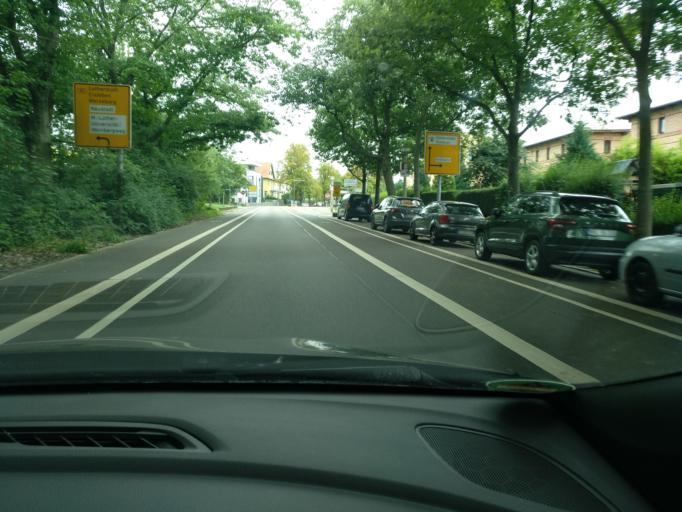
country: DE
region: Saxony-Anhalt
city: Halle Neustadt
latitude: 51.5009
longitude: 11.9424
